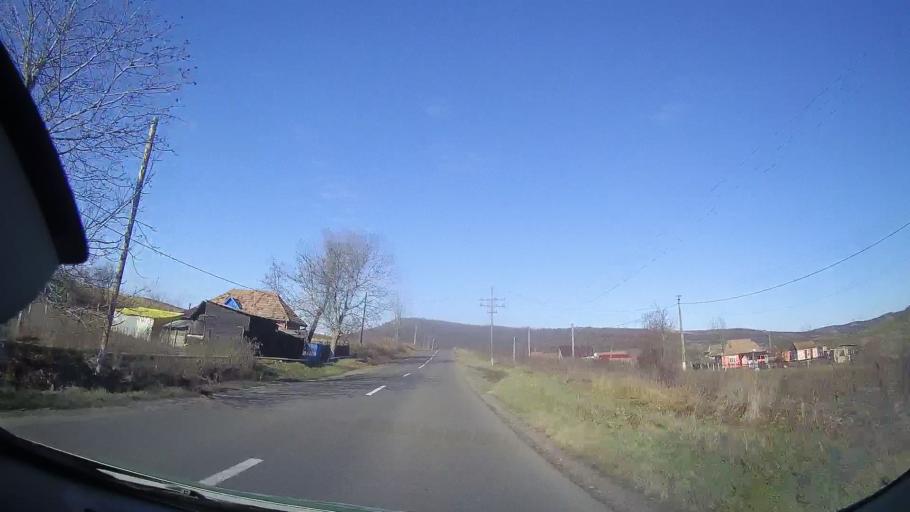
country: RO
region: Mures
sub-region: Comuna Mihesu de Campie
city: Mihesu de Campie
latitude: 46.6636
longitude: 24.1743
